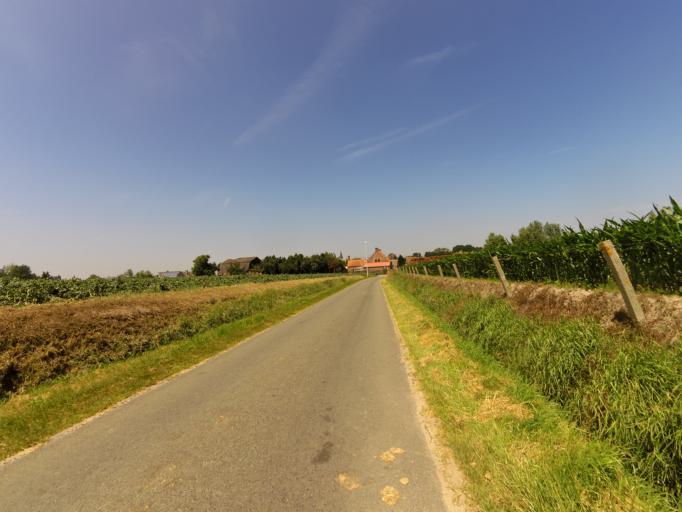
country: BE
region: Flanders
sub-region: Provincie West-Vlaanderen
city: Zedelgem
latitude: 51.1660
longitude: 3.1267
